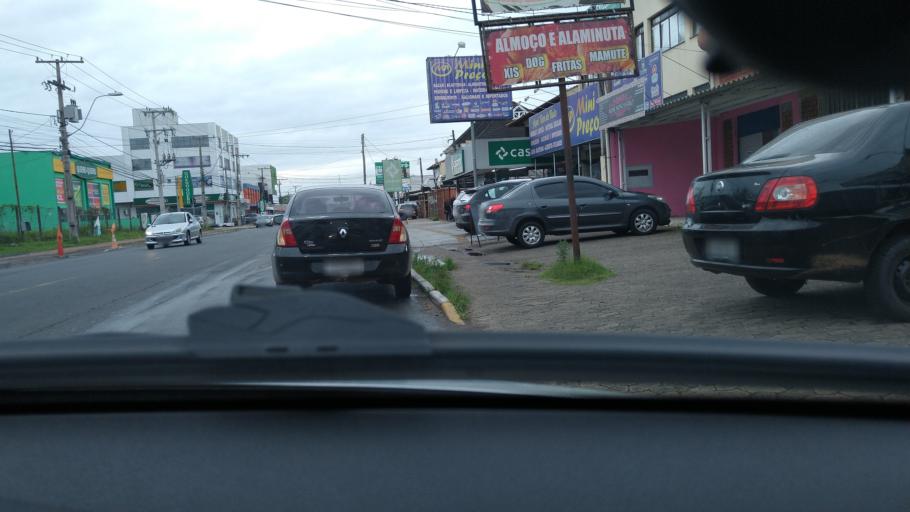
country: BR
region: Rio Grande do Sul
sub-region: Canoas
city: Canoas
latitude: -29.9025
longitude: -51.1958
